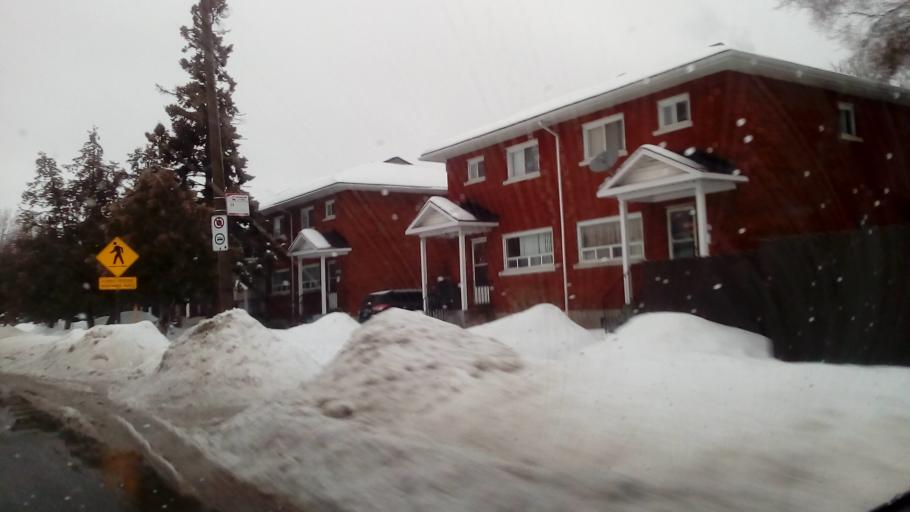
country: CA
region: Ontario
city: Ottawa
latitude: 45.4395
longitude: -75.6389
